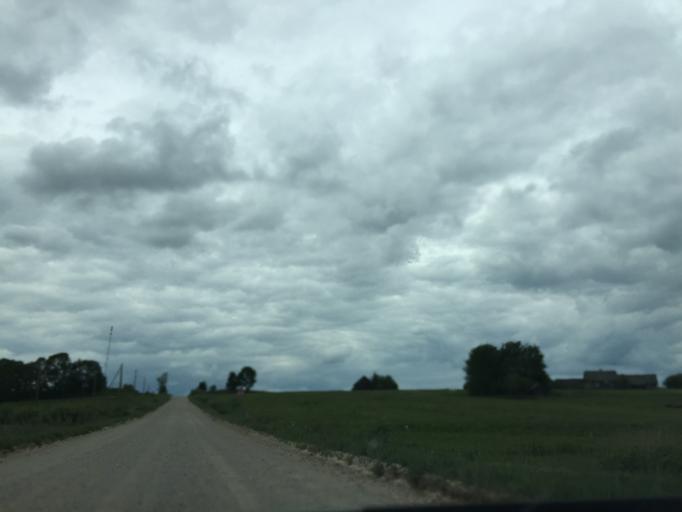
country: LV
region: Dagda
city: Dagda
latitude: 56.0114
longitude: 27.6021
